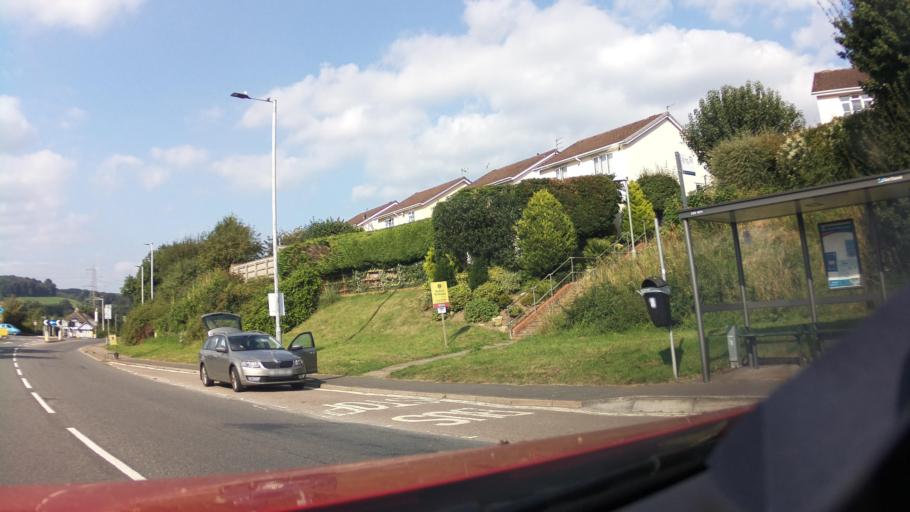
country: GB
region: England
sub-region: Devon
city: Exeter
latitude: 50.7459
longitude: -3.5477
